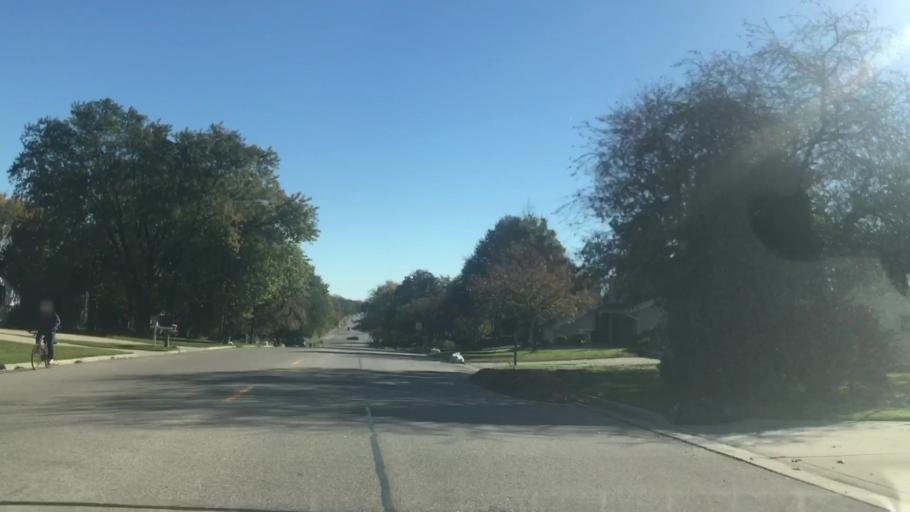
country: US
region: Wisconsin
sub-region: Waukesha County
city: Menomonee Falls
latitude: 43.1701
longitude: -88.1376
